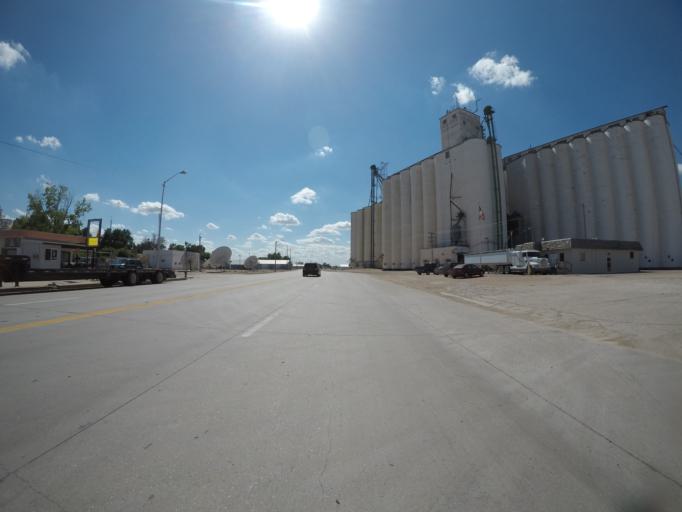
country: US
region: Colorado
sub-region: Phillips County
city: Holyoke
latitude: 40.5856
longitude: -102.3046
